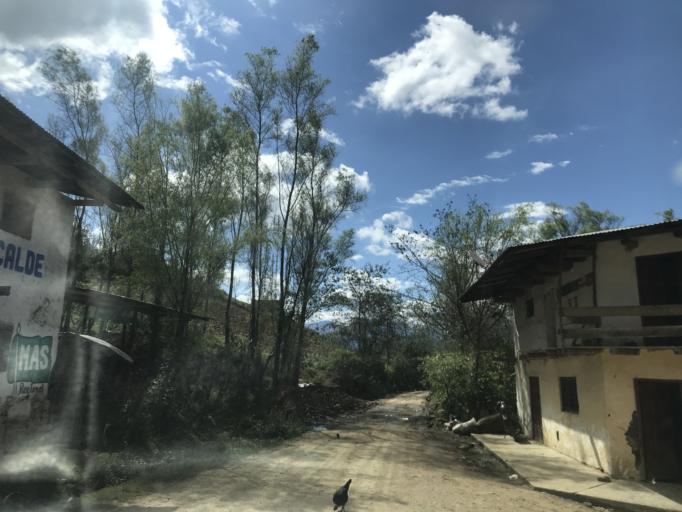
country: PE
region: Cajamarca
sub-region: Provincia de Chota
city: Querocoto
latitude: -6.3343
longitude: -79.0694
